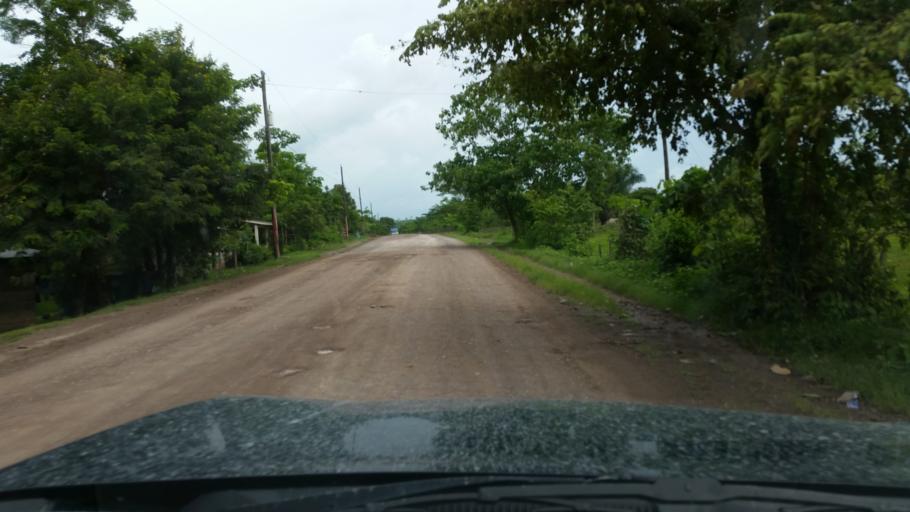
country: NI
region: Atlantico Norte (RAAN)
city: Siuna
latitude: 13.4875
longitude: -84.8447
